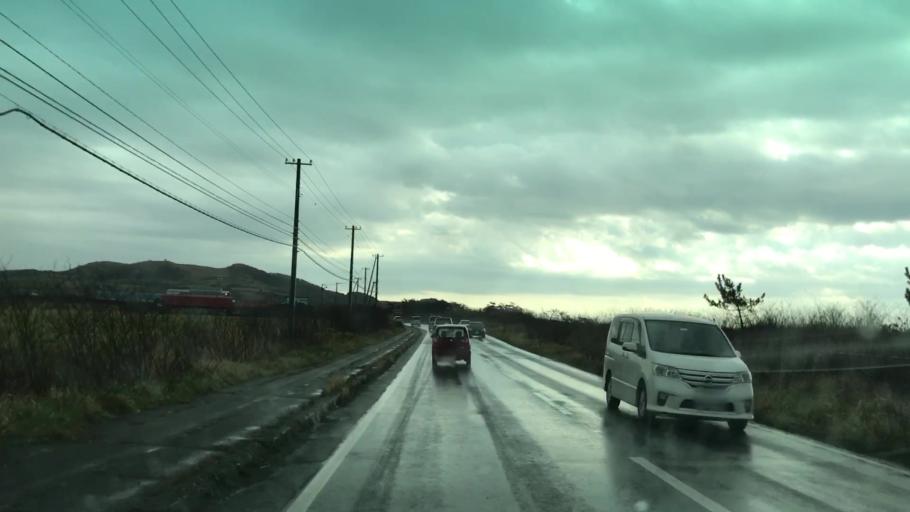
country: JP
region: Hokkaido
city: Shizunai-furukawacho
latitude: 42.1940
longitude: 142.6851
